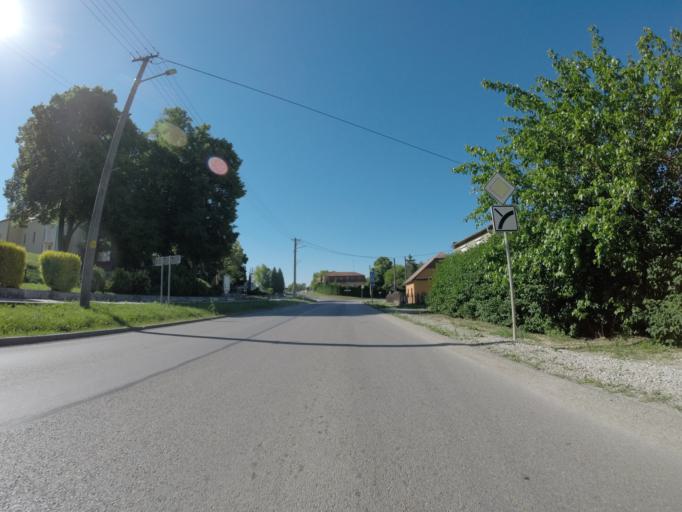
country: SK
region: Trnavsky
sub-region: Okres Trnava
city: Piestany
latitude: 48.5007
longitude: 17.9831
